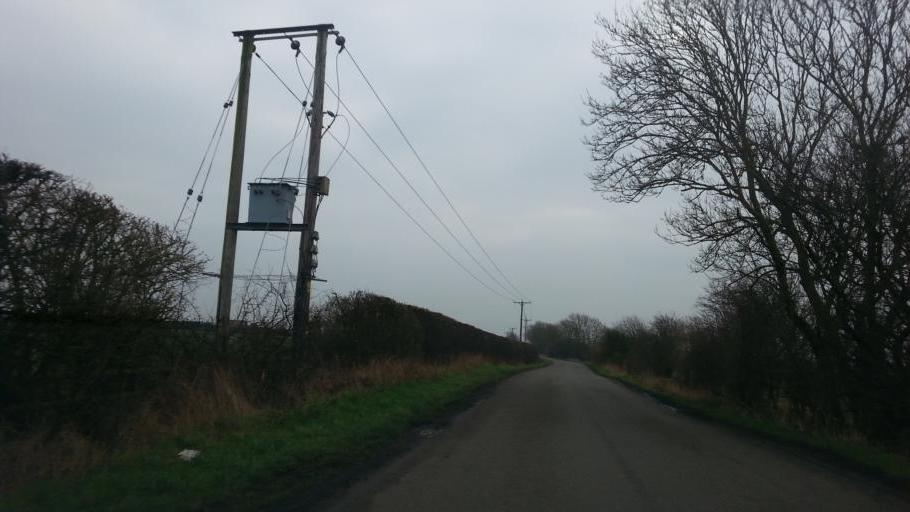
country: GB
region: England
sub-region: Lincolnshire
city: Long Bennington
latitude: 53.0056
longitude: -0.7986
